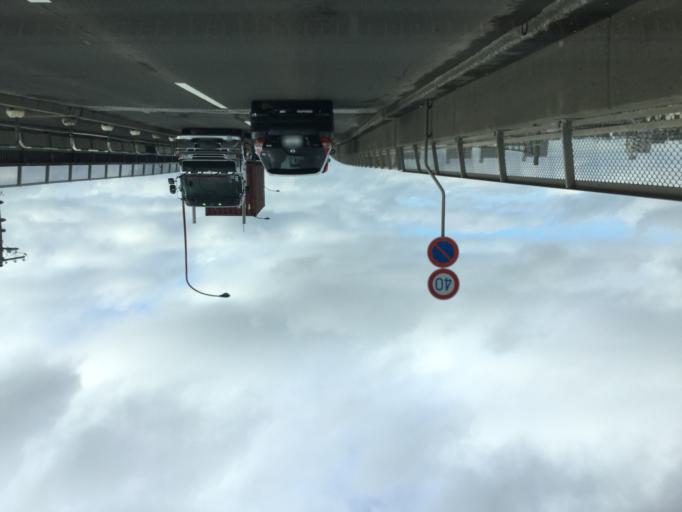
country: JP
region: Hokkaido
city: Ebetsu
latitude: 43.0431
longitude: 141.4598
